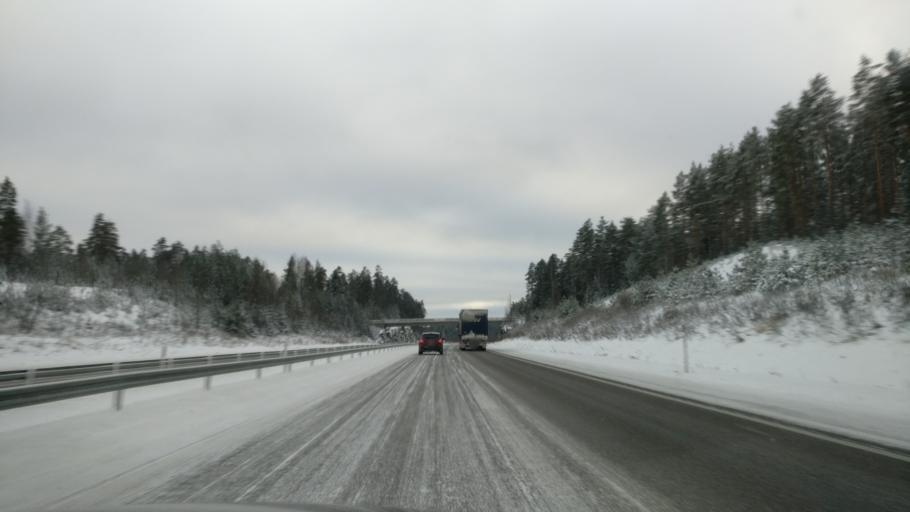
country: FI
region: Paijanne Tavastia
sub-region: Lahti
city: Nastola
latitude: 61.0122
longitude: 25.8205
